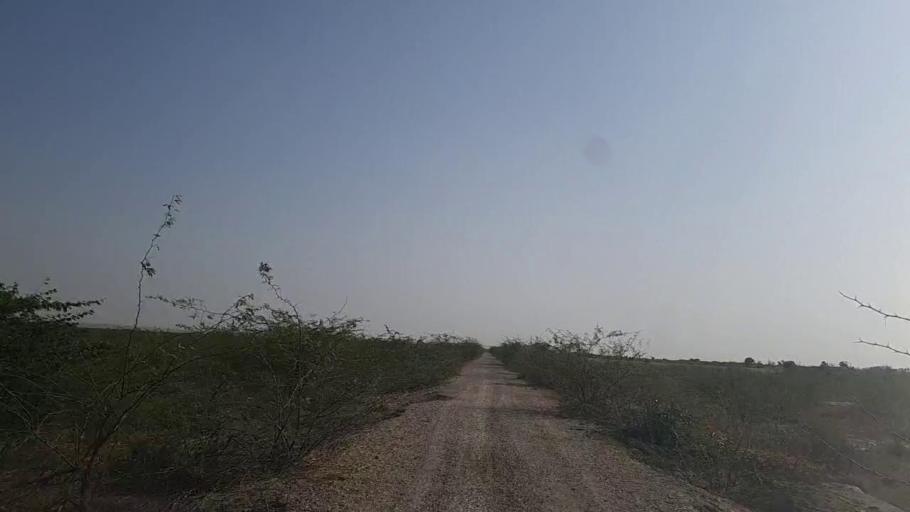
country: PK
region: Sindh
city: Kadhan
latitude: 24.5909
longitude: 69.2627
